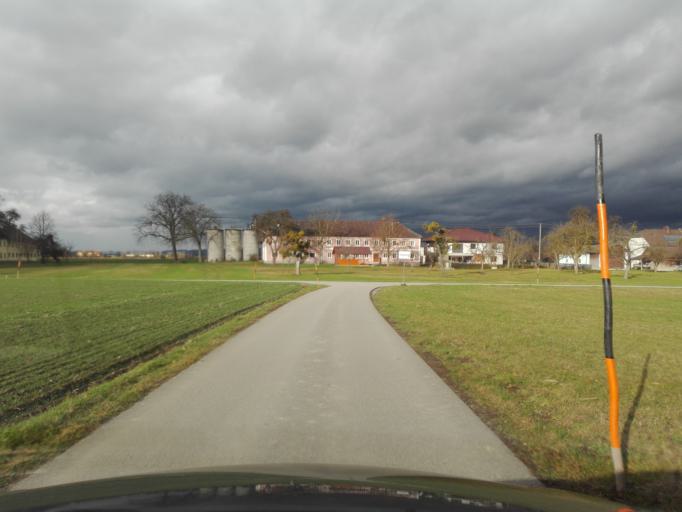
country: AT
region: Lower Austria
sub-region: Politischer Bezirk Amstetten
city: Strengberg
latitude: 48.1807
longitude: 14.6881
